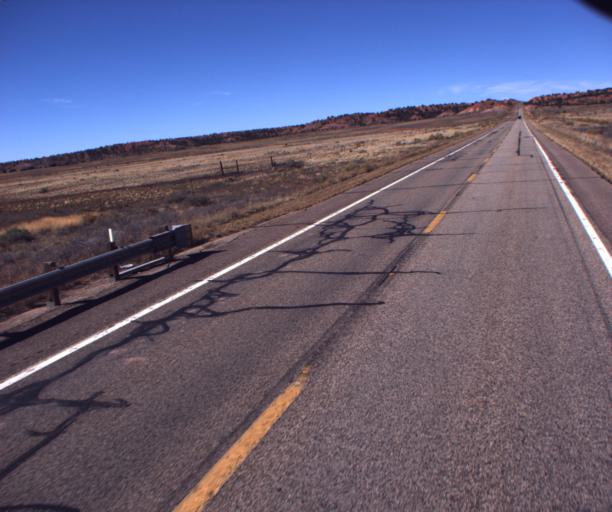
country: US
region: Arizona
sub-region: Mohave County
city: Colorado City
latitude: 36.8765
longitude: -112.8776
